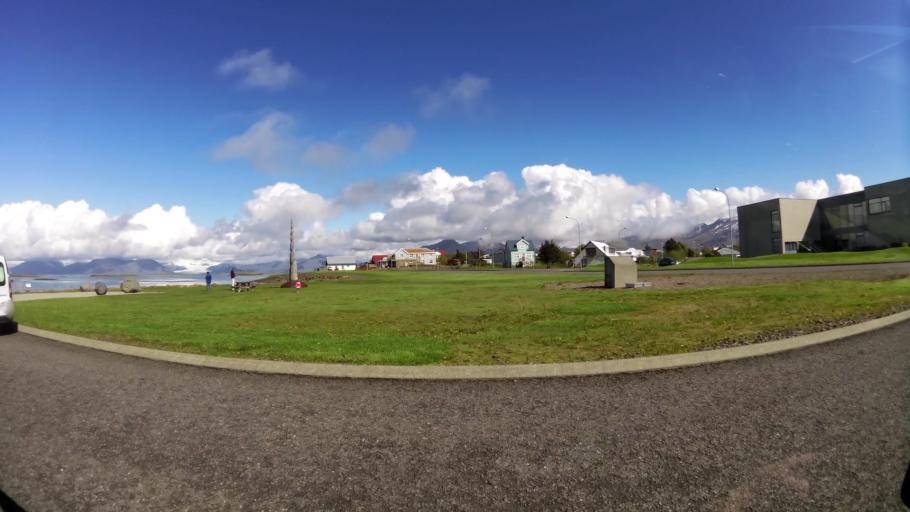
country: IS
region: East
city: Hoefn
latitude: 64.2527
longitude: -15.2140
